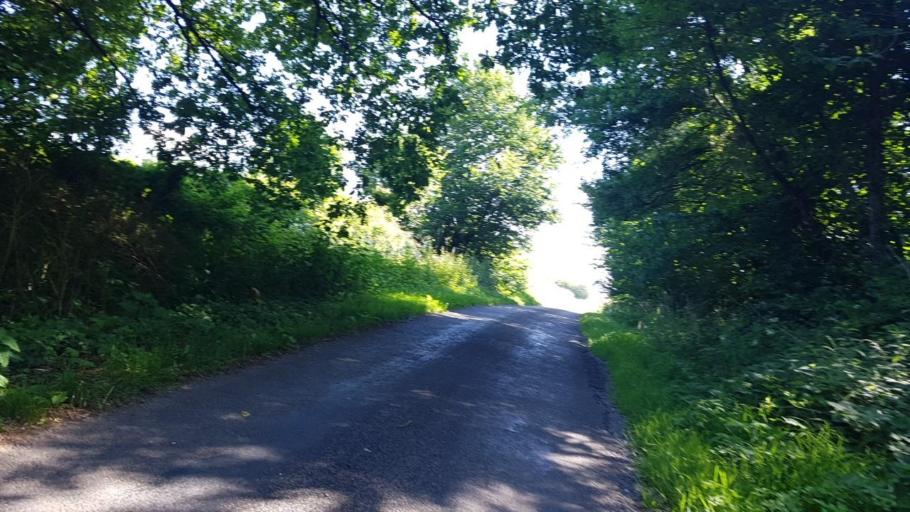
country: BE
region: Wallonia
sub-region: Province du Hainaut
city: Momignies
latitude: 50.0048
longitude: 4.1390
